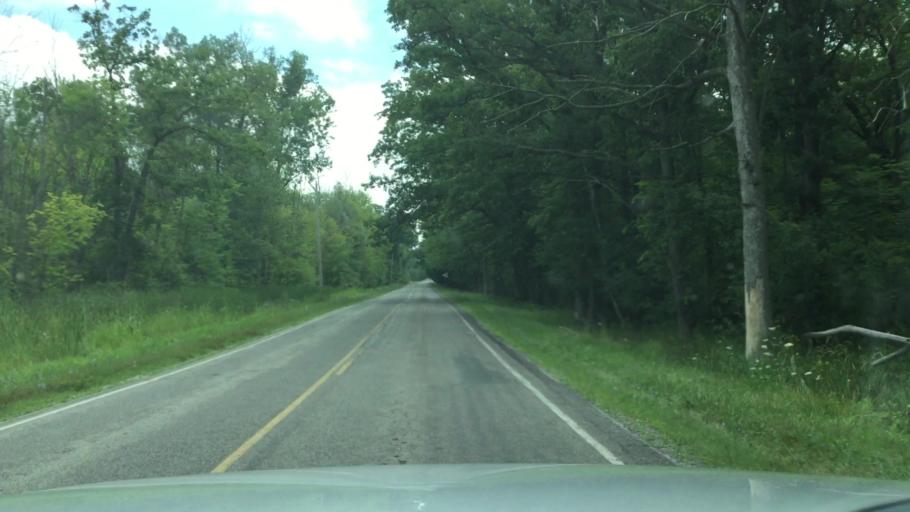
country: US
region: Michigan
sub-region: Saginaw County
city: Birch Run
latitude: 43.2943
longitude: -83.8318
